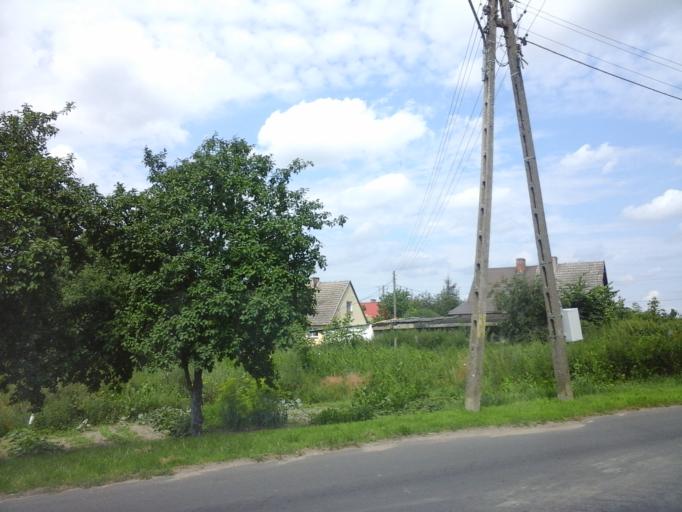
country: PL
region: West Pomeranian Voivodeship
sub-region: Powiat choszczenski
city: Recz
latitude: 53.2885
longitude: 15.4962
